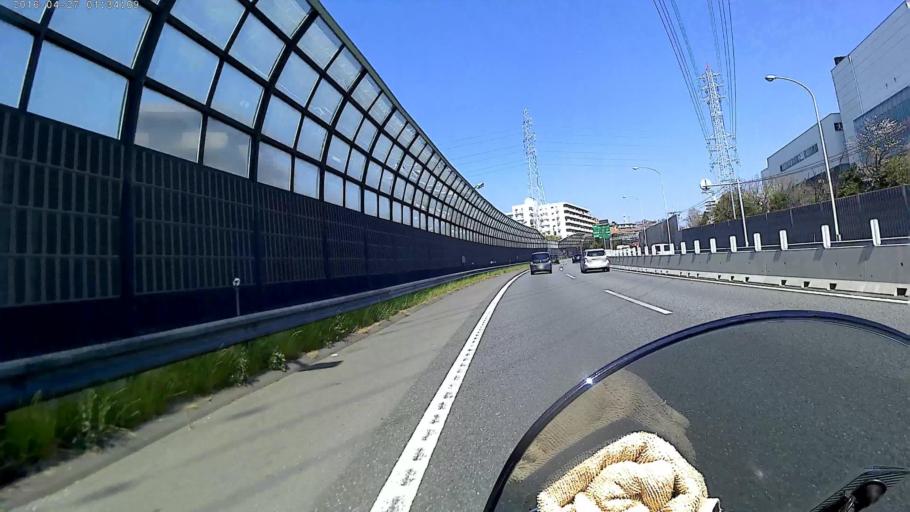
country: JP
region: Kanagawa
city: Yokohama
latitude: 35.4249
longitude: 139.5406
